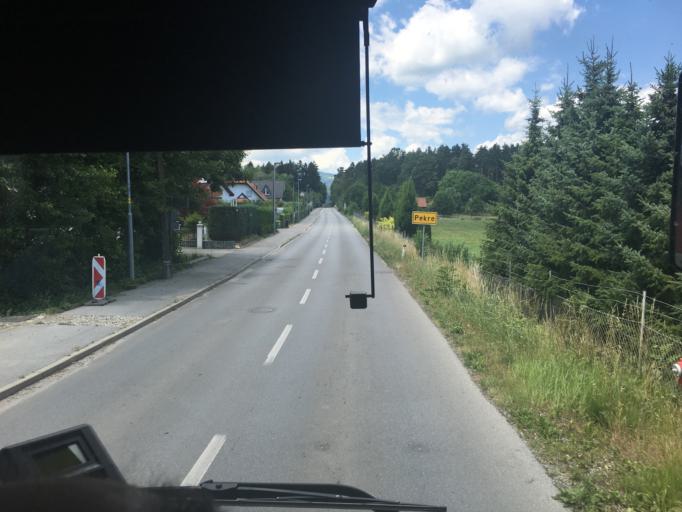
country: SI
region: Maribor
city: Pekre
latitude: 46.5423
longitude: 15.6042
